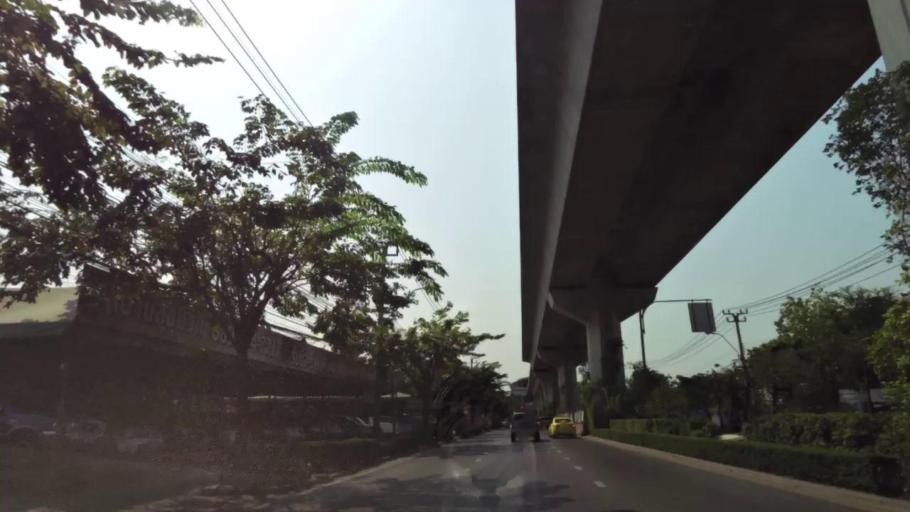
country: TH
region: Bangkok
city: Phra Khanong
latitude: 13.6638
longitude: 100.6029
